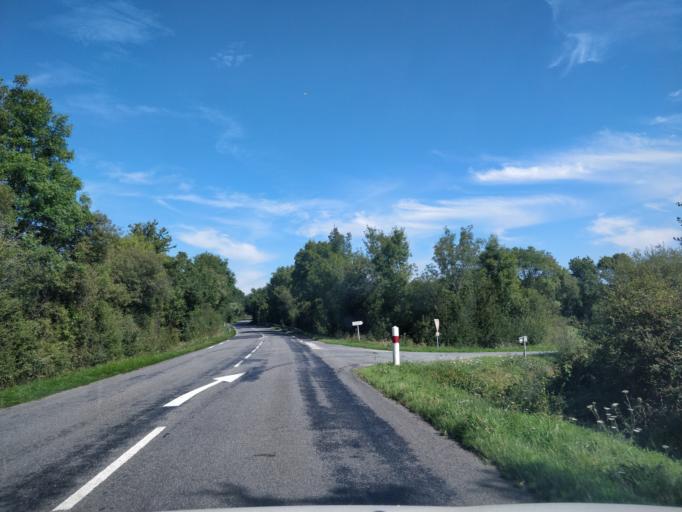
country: FR
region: Pays de la Loire
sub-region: Departement de la Loire-Atlantique
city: Quilly
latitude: 47.4466
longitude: -1.9259
